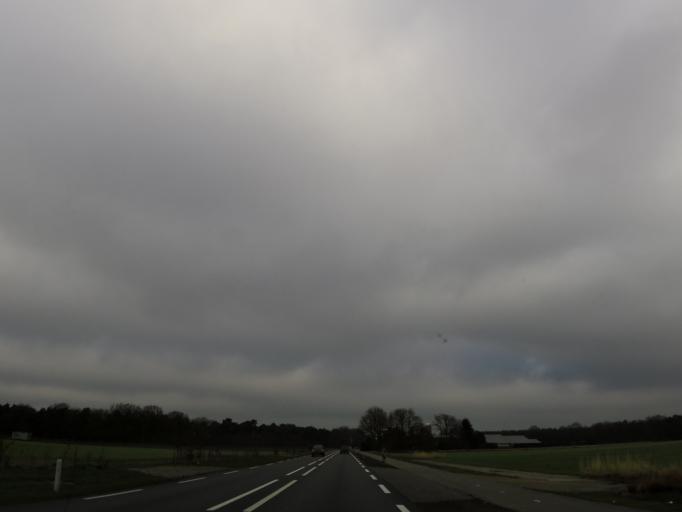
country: NL
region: Limburg
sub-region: Gemeente Peel en Maas
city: Maasbree
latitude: 51.3542
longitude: 5.9731
